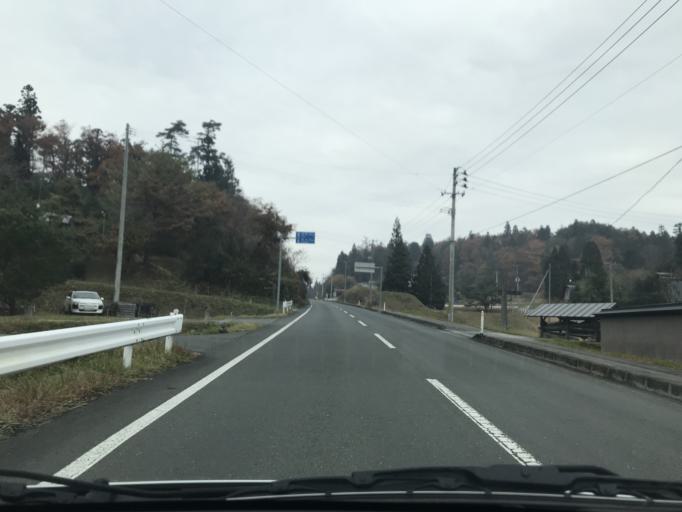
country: JP
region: Iwate
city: Mizusawa
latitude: 39.1624
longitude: 141.2024
